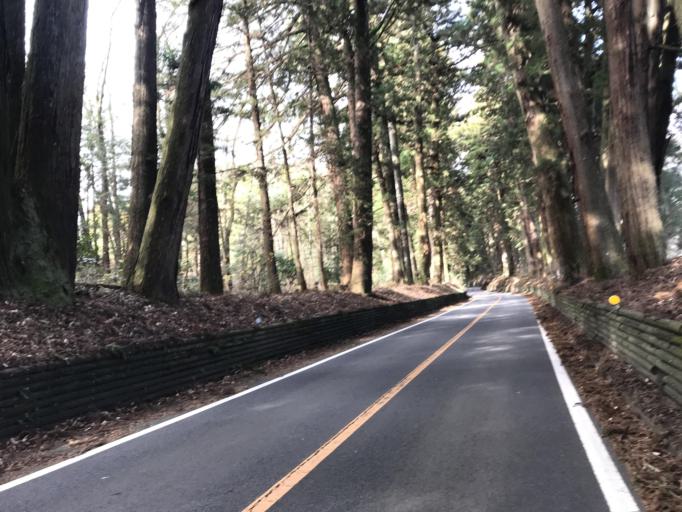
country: JP
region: Tochigi
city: Imaichi
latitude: 36.6914
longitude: 139.7163
